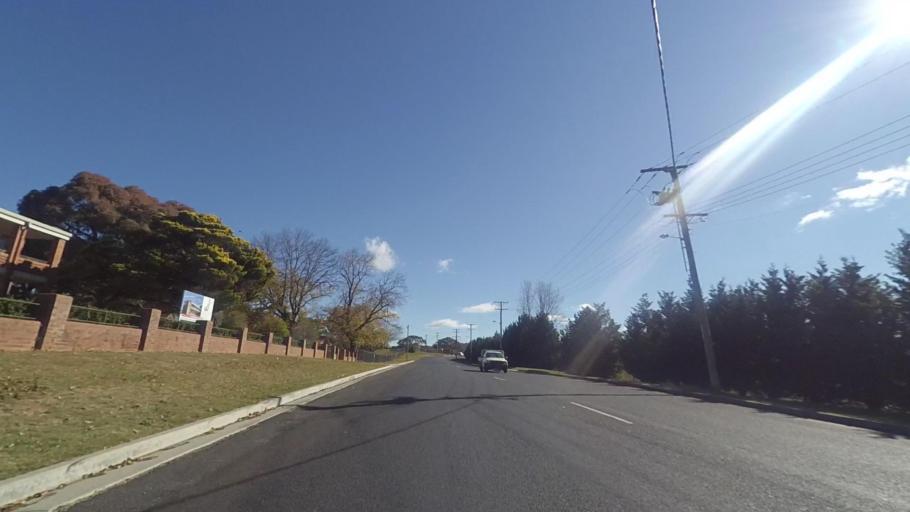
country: AU
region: New South Wales
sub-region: Bathurst Regional
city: Bathurst
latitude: -33.4384
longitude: 149.5661
